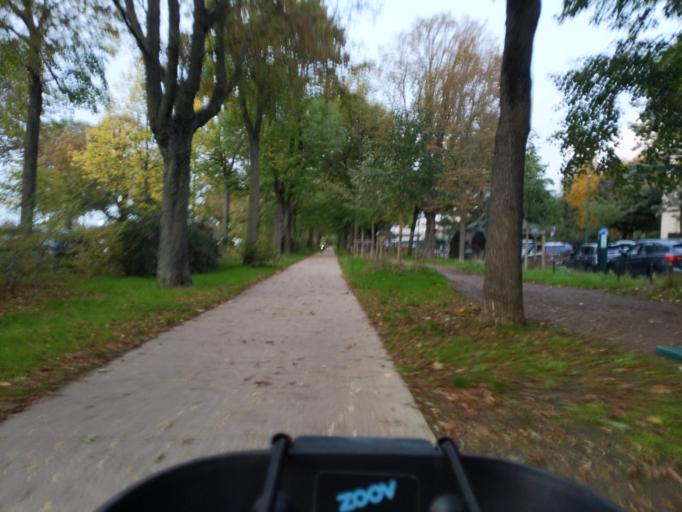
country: FR
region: Ile-de-France
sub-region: Departement des Hauts-de-Seine
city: Boulogne-Billancourt
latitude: 48.8525
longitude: 2.2600
